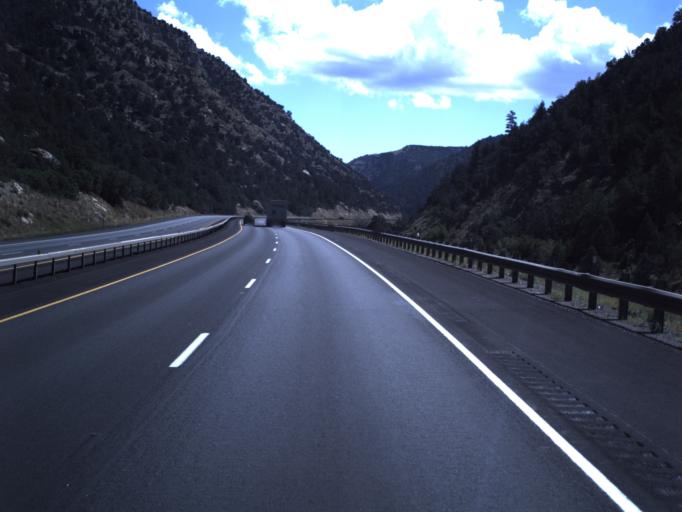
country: US
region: Utah
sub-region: Sevier County
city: Salina
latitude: 38.8931
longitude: -111.6204
